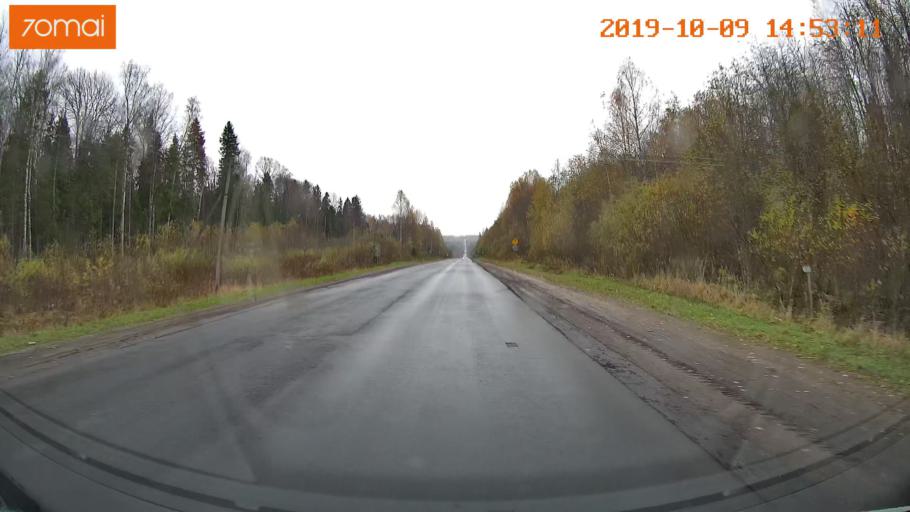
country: RU
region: Kostroma
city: Chistyye Bory
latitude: 58.3709
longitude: 41.6370
